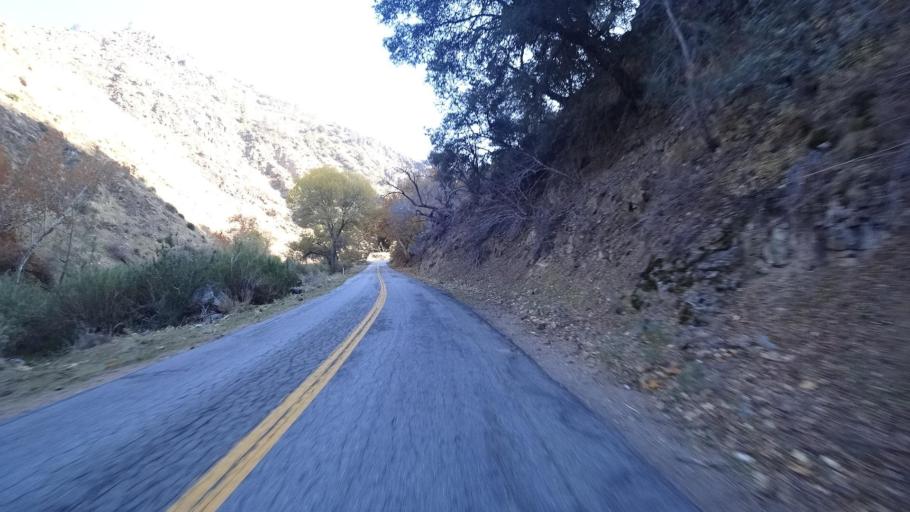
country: US
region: California
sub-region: Kern County
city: Golden Hills
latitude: 35.3069
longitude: -118.4947
